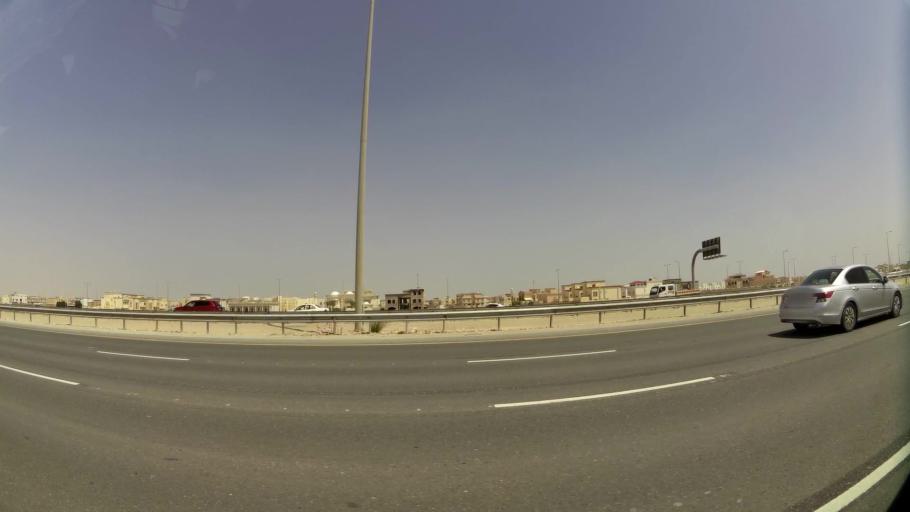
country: QA
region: Baladiyat Umm Salal
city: Umm Salal Muhammad
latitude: 25.3950
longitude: 51.4323
